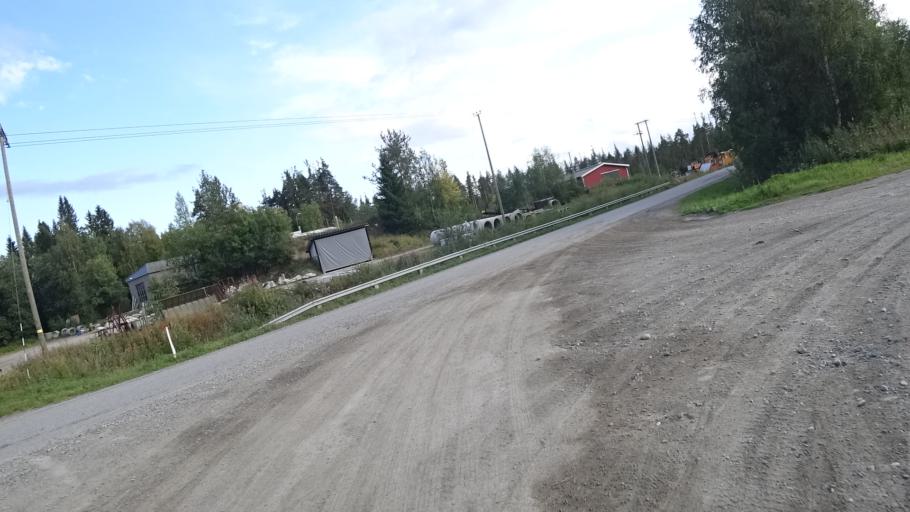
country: FI
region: North Karelia
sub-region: Joensuu
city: Ilomantsi
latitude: 62.6697
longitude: 30.9530
